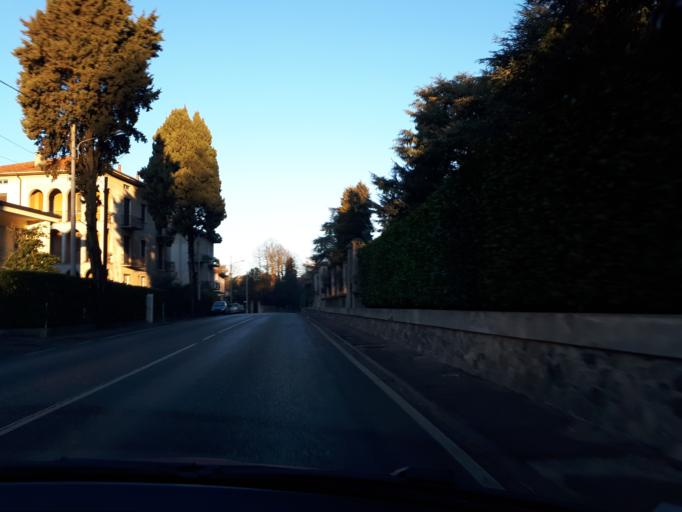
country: IT
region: Lombardy
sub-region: Provincia di Como
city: Fino Mornasco
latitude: 45.7388
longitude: 9.0537
